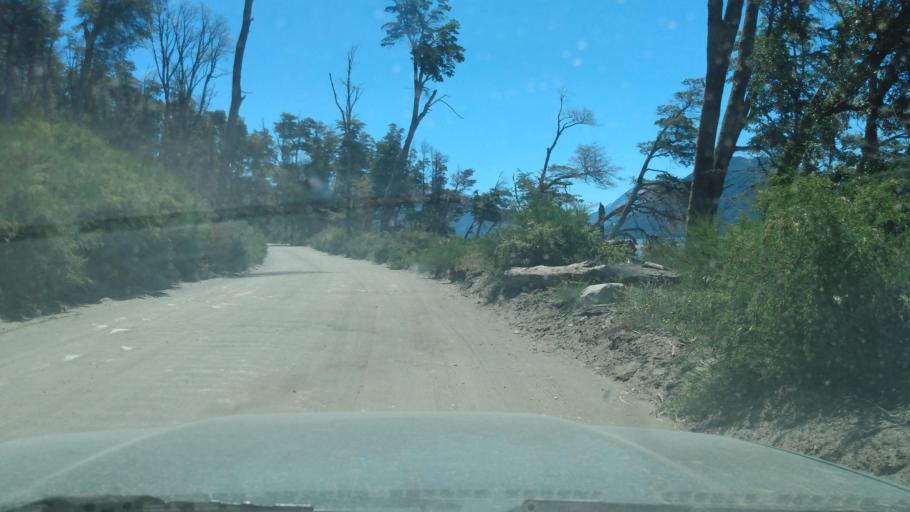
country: AR
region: Neuquen
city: Villa La Angostura
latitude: -40.6448
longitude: -71.4397
